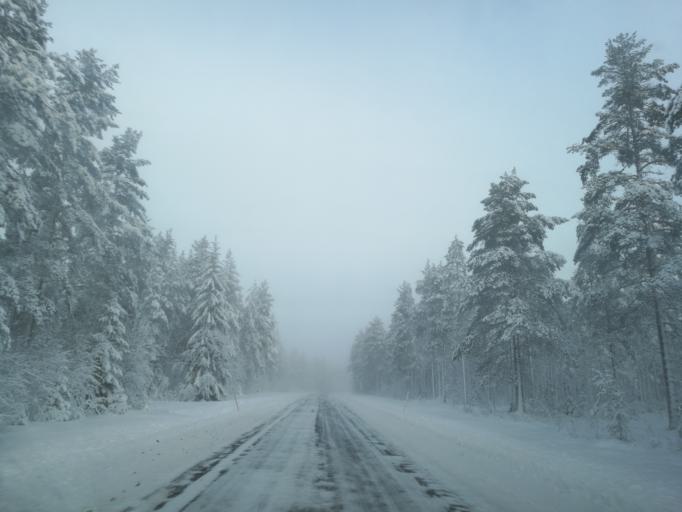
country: SE
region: Vaermland
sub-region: Torsby Kommun
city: Torsby
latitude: 60.6361
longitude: 12.6959
